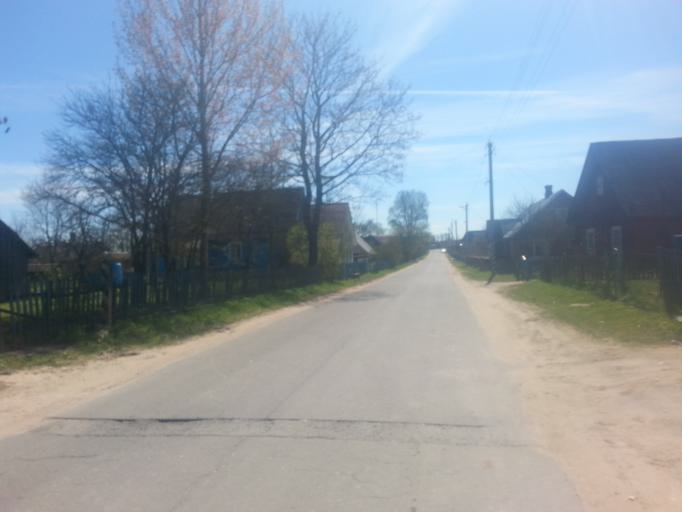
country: BY
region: Minsk
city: Narach
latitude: 54.9399
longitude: 26.6914
